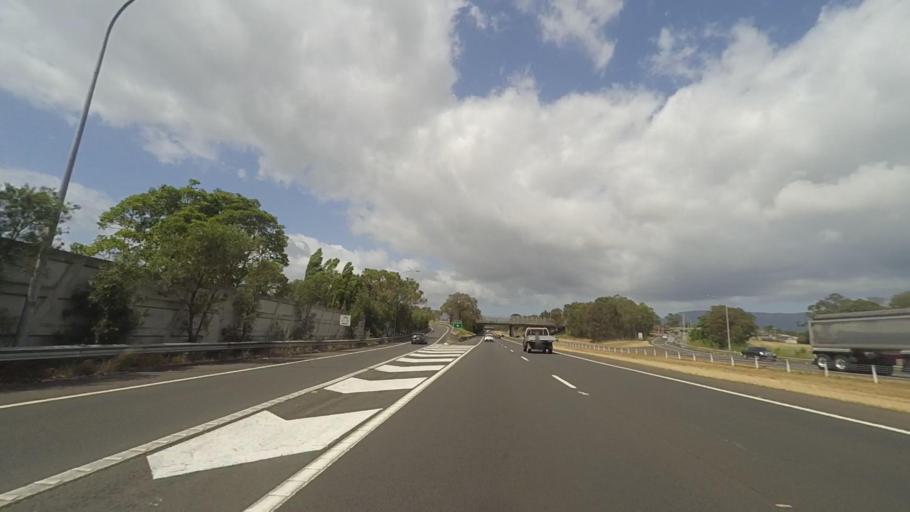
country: AU
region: New South Wales
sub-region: Wollongong
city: Koonawarra
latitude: -34.4979
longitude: 150.7982
